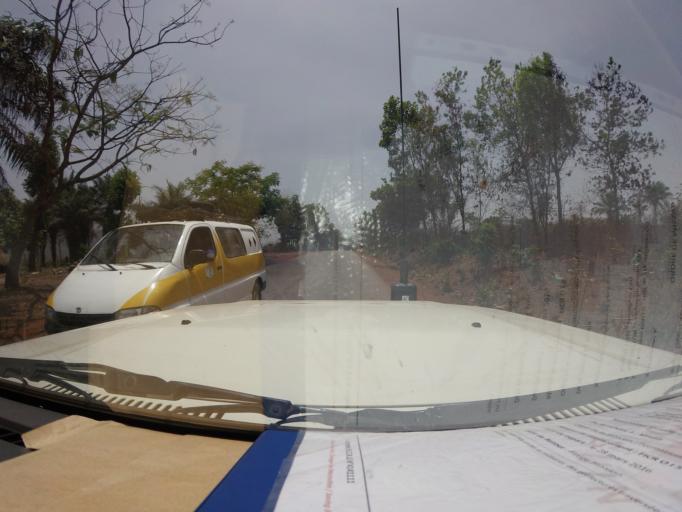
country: GN
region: Kindia
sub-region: Coyah
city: Coyah
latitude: 9.7989
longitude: -13.2890
